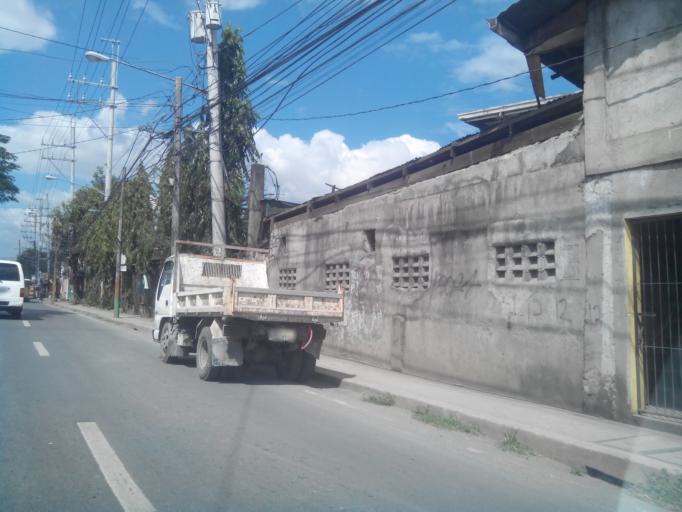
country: PH
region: Calabarzon
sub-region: Province of Rizal
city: Taytay
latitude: 14.5481
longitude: 121.1415
